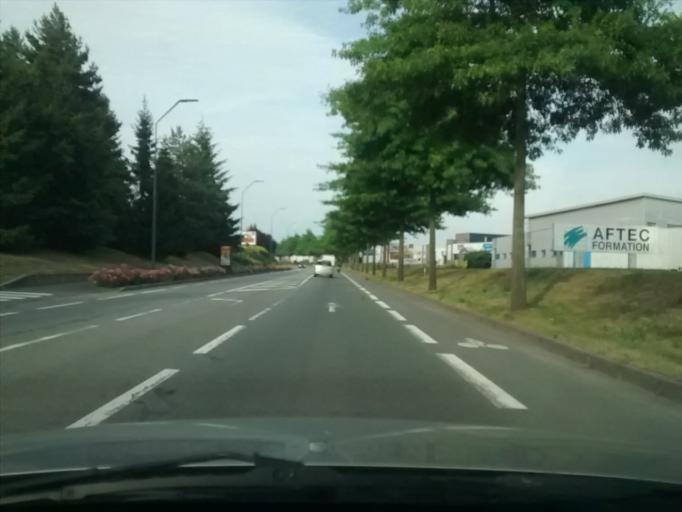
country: FR
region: Brittany
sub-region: Departement d'Ille-et-Vilaine
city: Vitre
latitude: 48.1148
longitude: -1.1939
